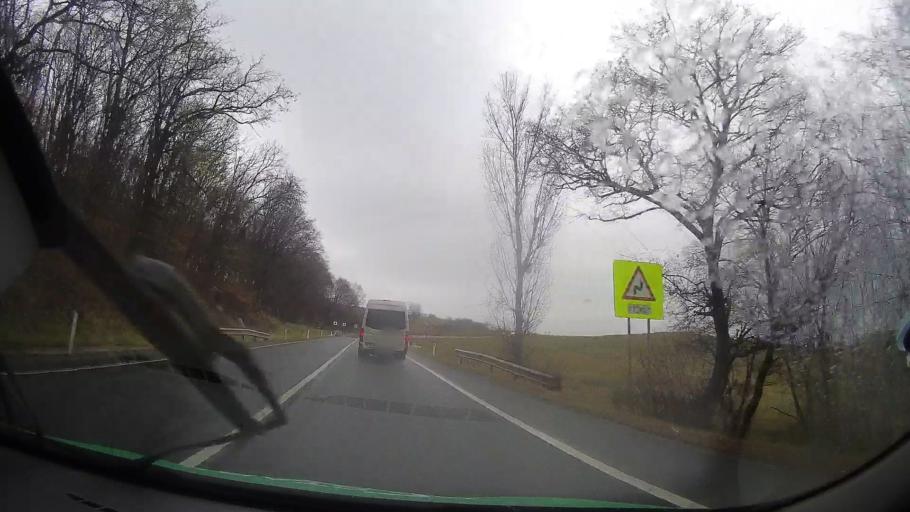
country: RO
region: Bistrita-Nasaud
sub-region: Comuna Galatii Bistritei
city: Galatii Bistritei
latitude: 47.0349
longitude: 24.4212
